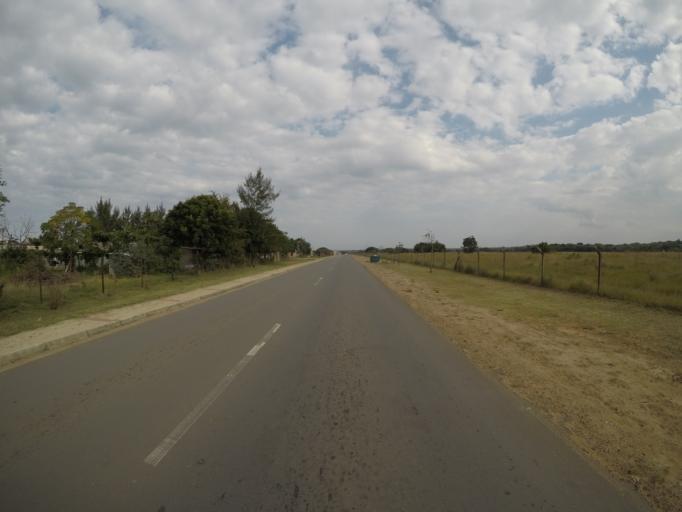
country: ZA
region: KwaZulu-Natal
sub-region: uThungulu District Municipality
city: Richards Bay
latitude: -28.7434
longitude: 32.0916
